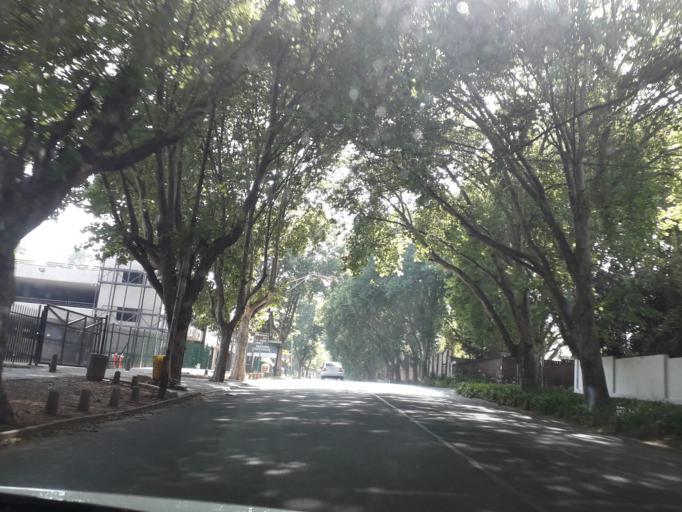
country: ZA
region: Gauteng
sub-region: City of Johannesburg Metropolitan Municipality
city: Johannesburg
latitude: -26.1700
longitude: 28.0366
